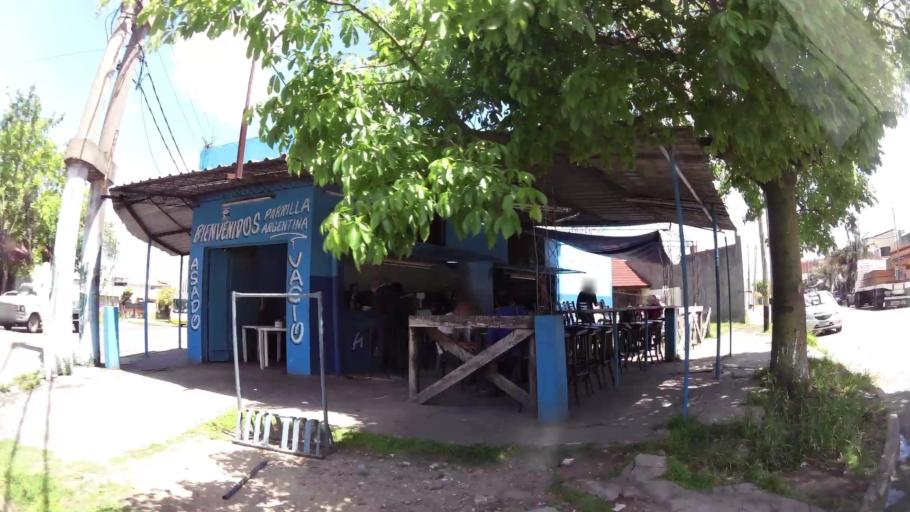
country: AR
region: Buenos Aires
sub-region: Partido de Lomas de Zamora
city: Lomas de Zamora
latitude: -34.7344
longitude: -58.4175
